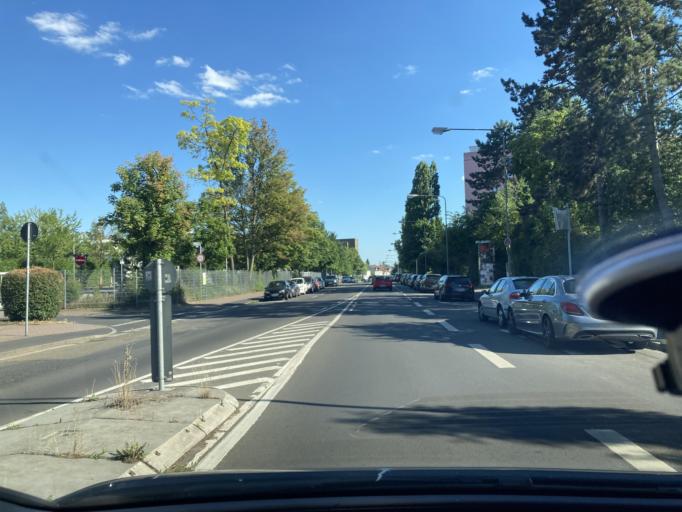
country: DE
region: Hesse
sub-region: Regierungsbezirk Darmstadt
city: Steinbach am Taunus
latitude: 50.1596
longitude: 8.6212
